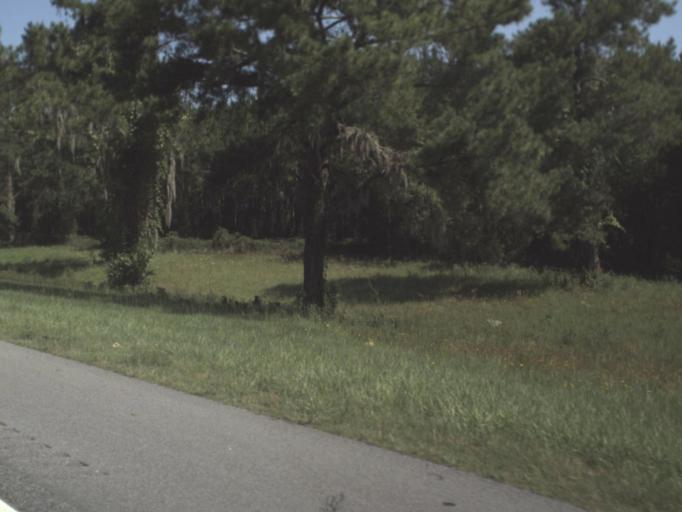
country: US
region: Florida
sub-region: Suwannee County
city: Live Oak
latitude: 30.3459
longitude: -82.9854
